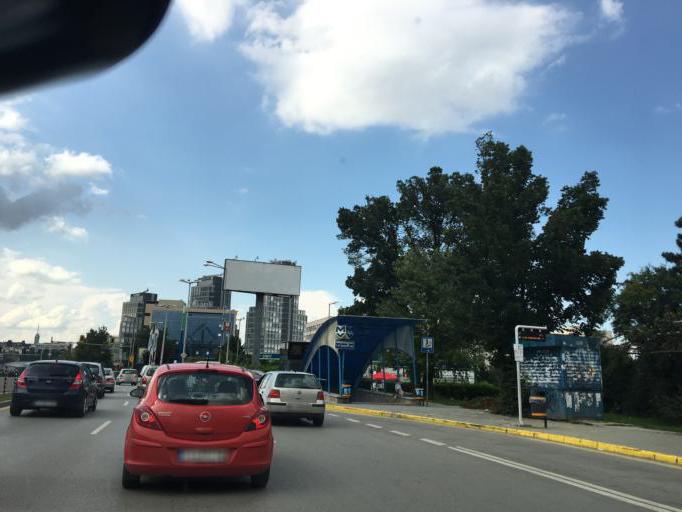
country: BG
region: Sofia-Capital
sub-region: Stolichna Obshtina
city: Sofia
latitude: 42.6624
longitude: 23.3586
